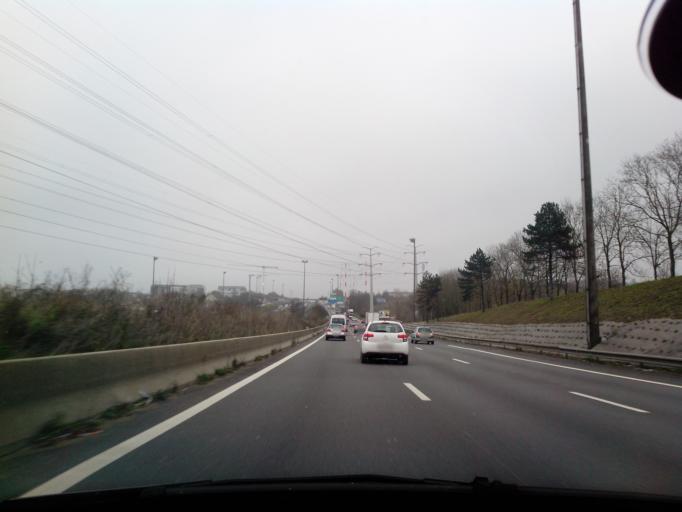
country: FR
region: Ile-de-France
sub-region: Departement de l'Essonne
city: Wissous
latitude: 48.7442
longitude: 2.3238
